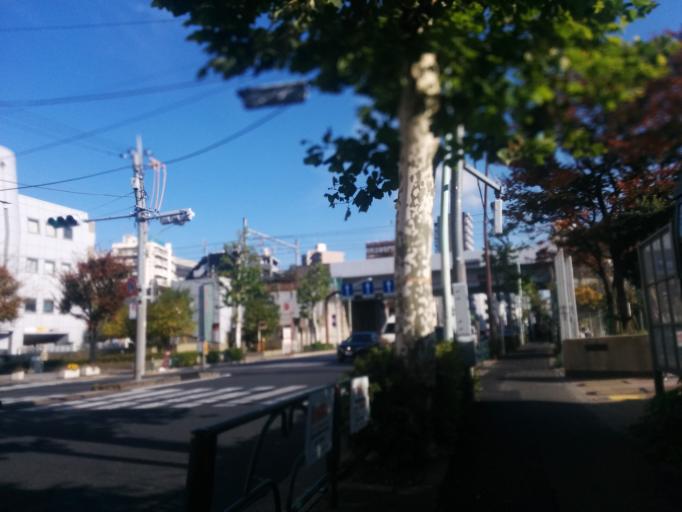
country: JP
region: Tokyo
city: Tokyo
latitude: 35.7162
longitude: 139.7040
